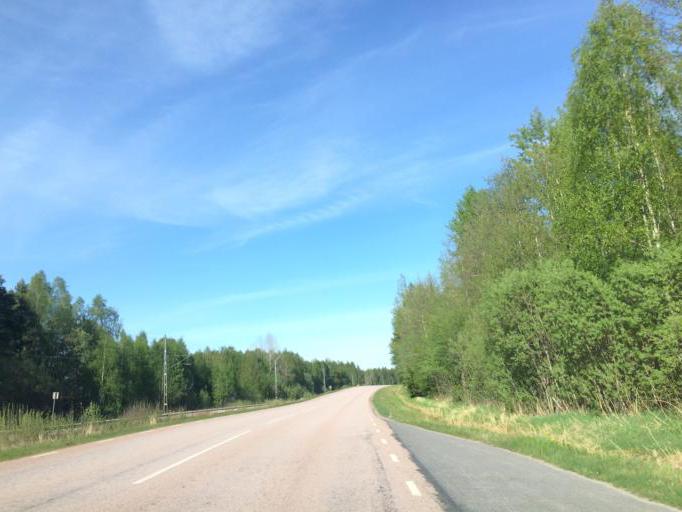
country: SE
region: Soedermanland
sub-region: Eskilstuna Kommun
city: Kvicksund
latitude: 59.4161
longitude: 16.2792
